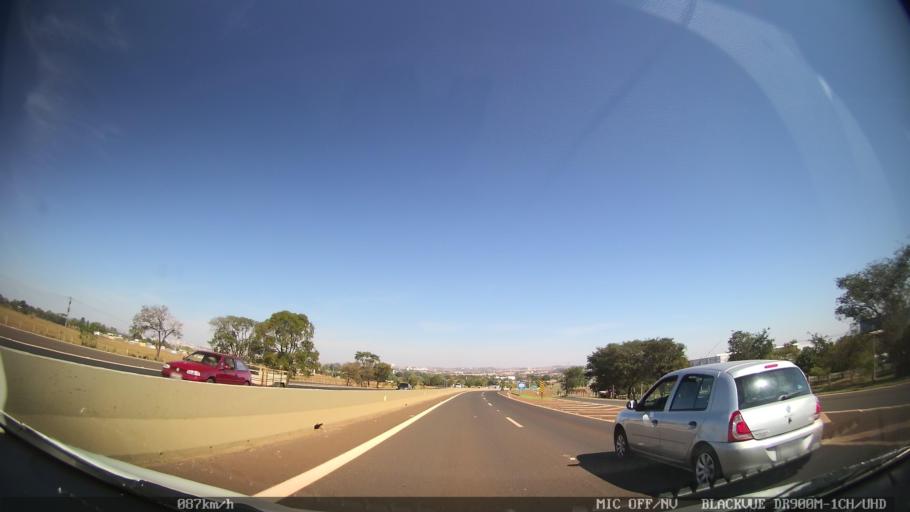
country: BR
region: Sao Paulo
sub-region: Ribeirao Preto
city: Ribeirao Preto
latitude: -21.0986
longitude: -47.7983
